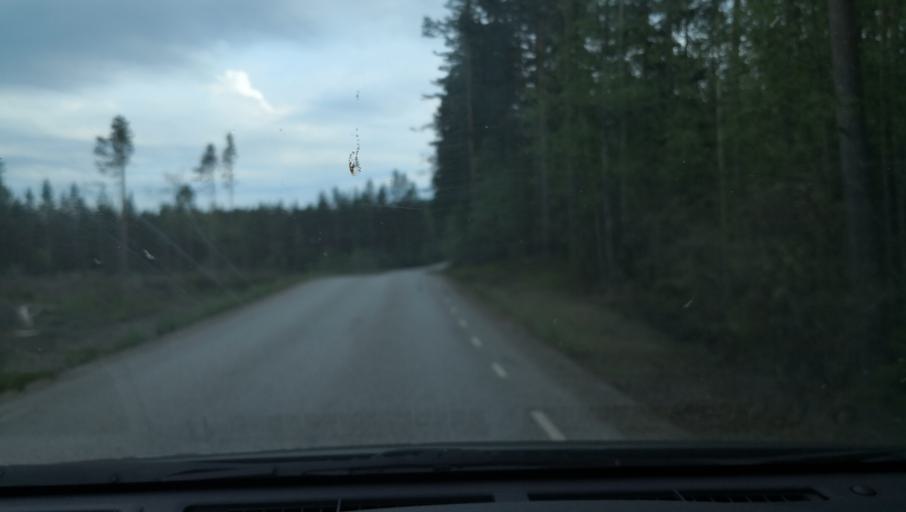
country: SE
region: Vaestmanland
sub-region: Skinnskattebergs Kommun
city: Skinnskatteberg
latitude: 59.8149
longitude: 15.5557
